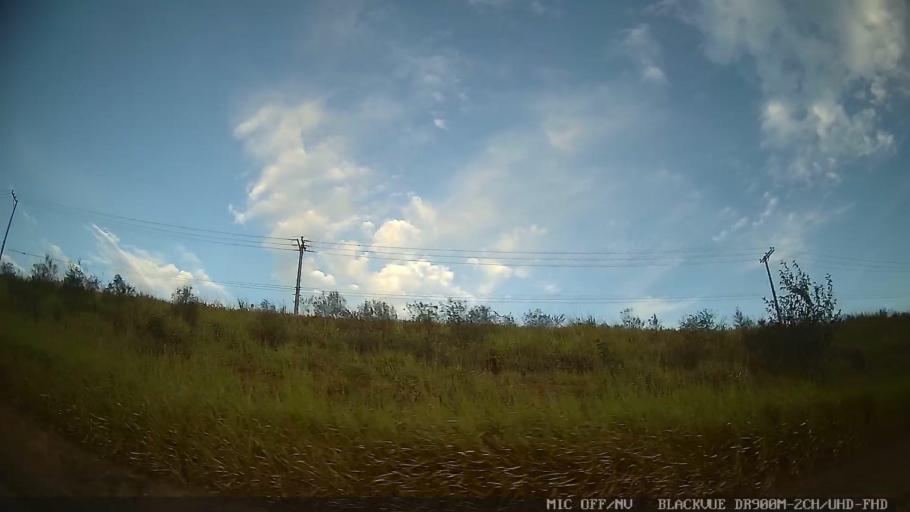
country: BR
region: Sao Paulo
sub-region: Salto
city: Salto
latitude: -23.1778
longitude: -47.2733
